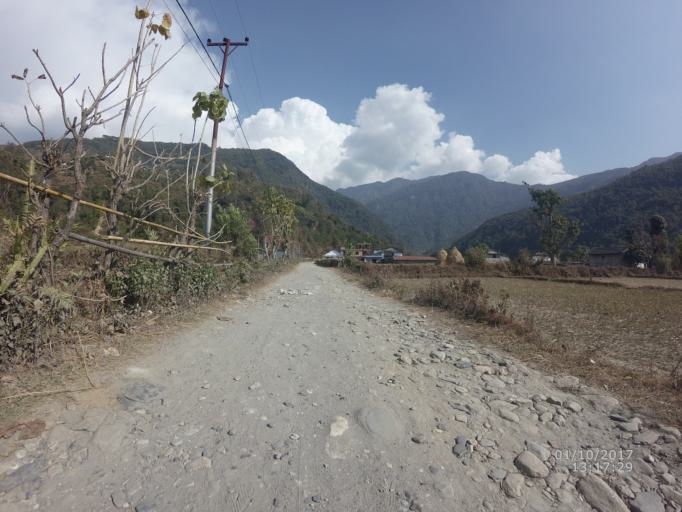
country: NP
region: Western Region
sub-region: Gandaki Zone
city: Pokhara
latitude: 28.3306
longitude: 83.9665
